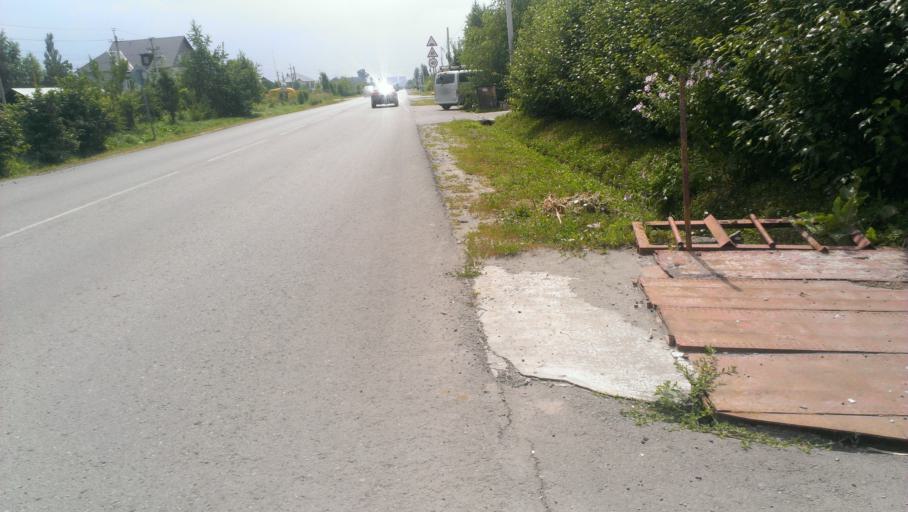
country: RU
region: Altai Krai
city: Novosilikatnyy
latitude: 53.3700
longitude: 83.6511
